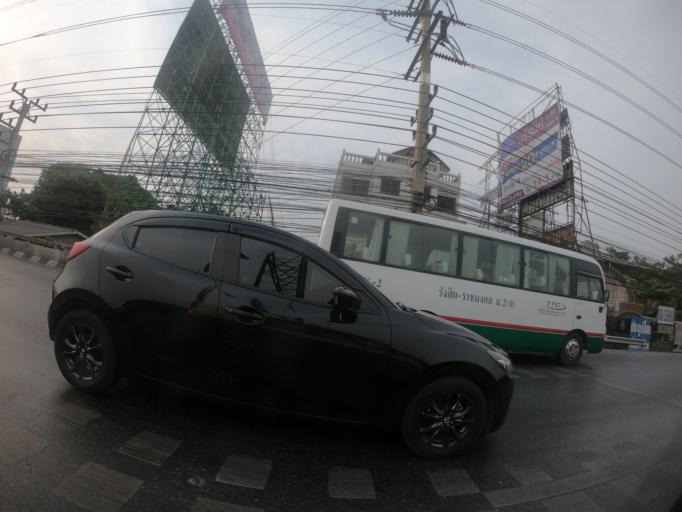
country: TH
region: Bangkok
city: Sai Mai
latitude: 13.9866
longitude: 100.6214
